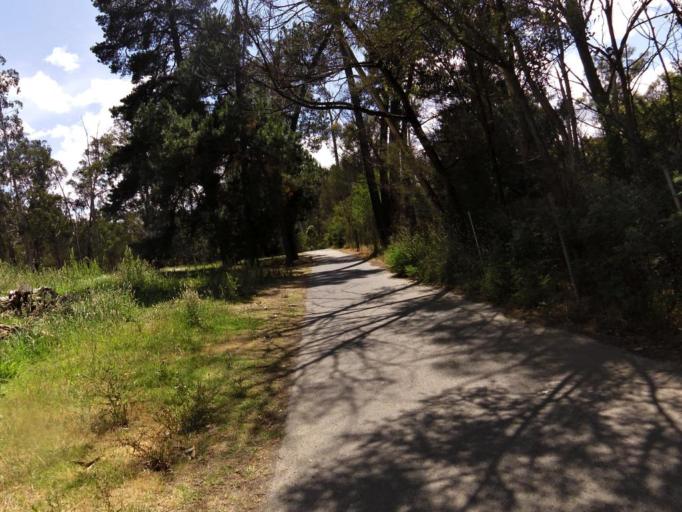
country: AU
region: Victoria
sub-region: Nillumbik
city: Eltham North
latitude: -37.6941
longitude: 145.1510
